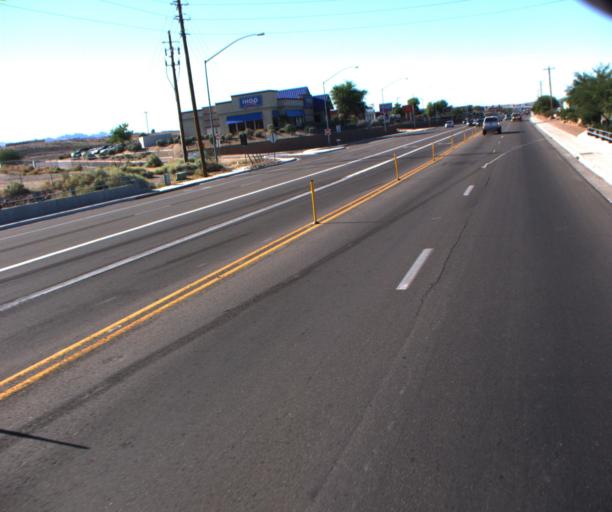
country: US
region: Nevada
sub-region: Clark County
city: Laughlin
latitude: 35.1714
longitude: -114.5660
